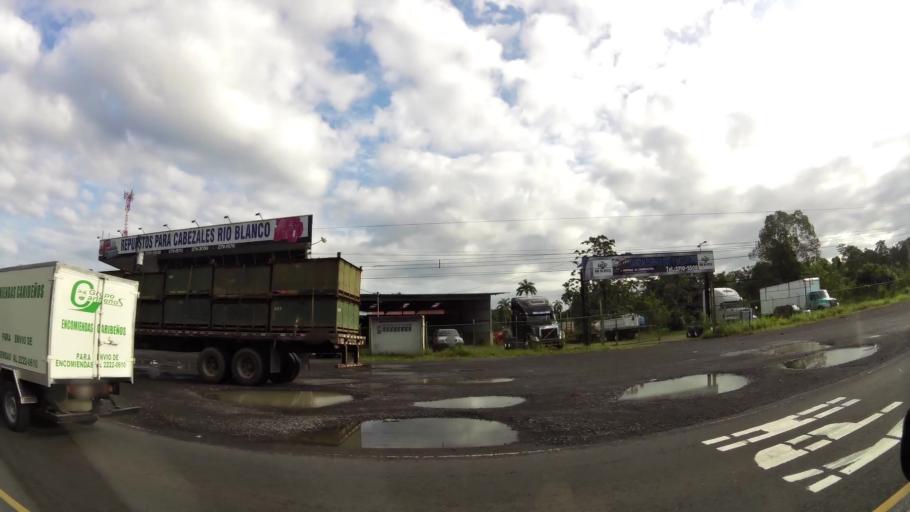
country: CR
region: Limon
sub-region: Canton de Pococi
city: Guapiles
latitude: 10.2110
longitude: -83.8361
